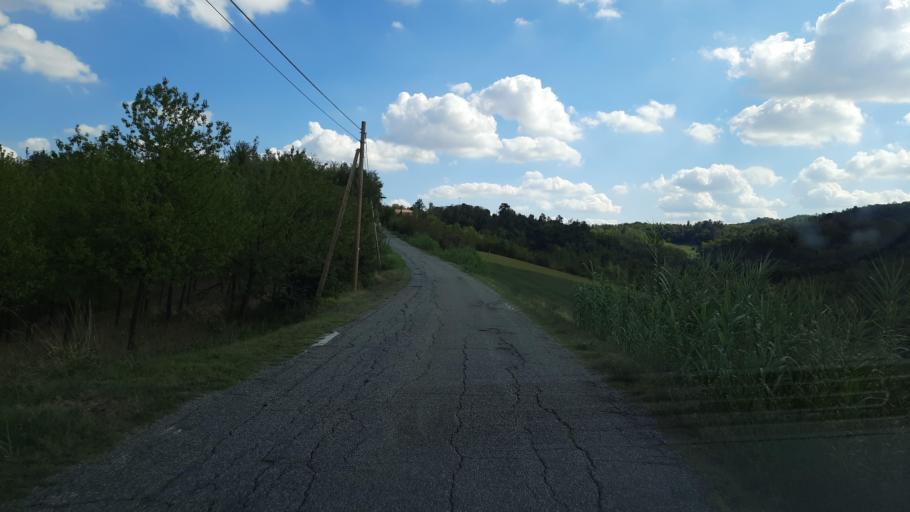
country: IT
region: Piedmont
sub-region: Provincia di Alessandria
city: Cereseto
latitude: 45.0728
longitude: 8.3284
